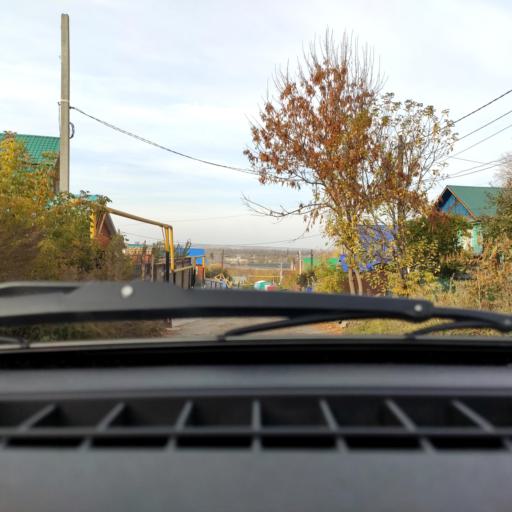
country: RU
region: Bashkortostan
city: Ufa
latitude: 54.7358
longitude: 55.9265
